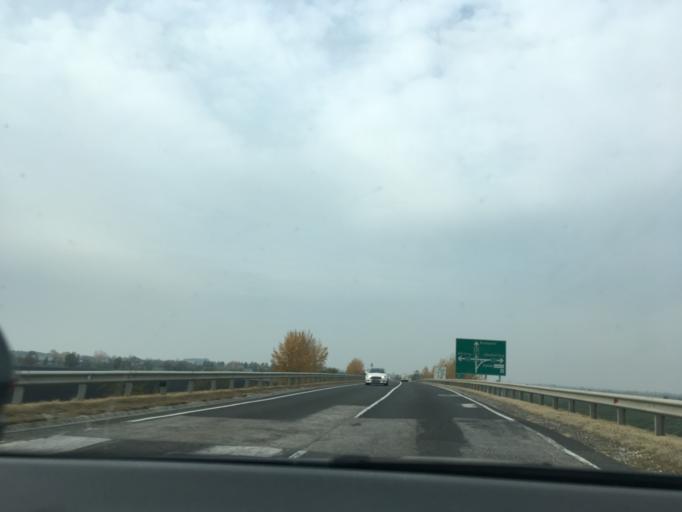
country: HU
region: Jasz-Nagykun-Szolnok
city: Toszeg
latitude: 47.1755
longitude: 20.1021
